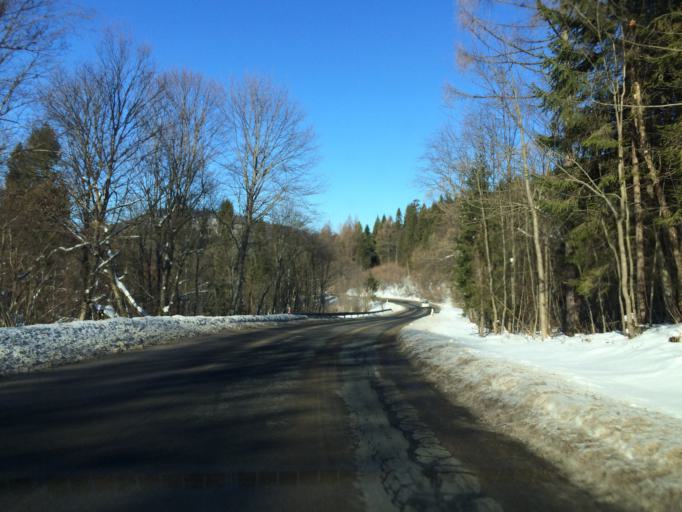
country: PL
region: Subcarpathian Voivodeship
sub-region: Powiat leski
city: Cisna
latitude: 49.1928
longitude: 22.3737
